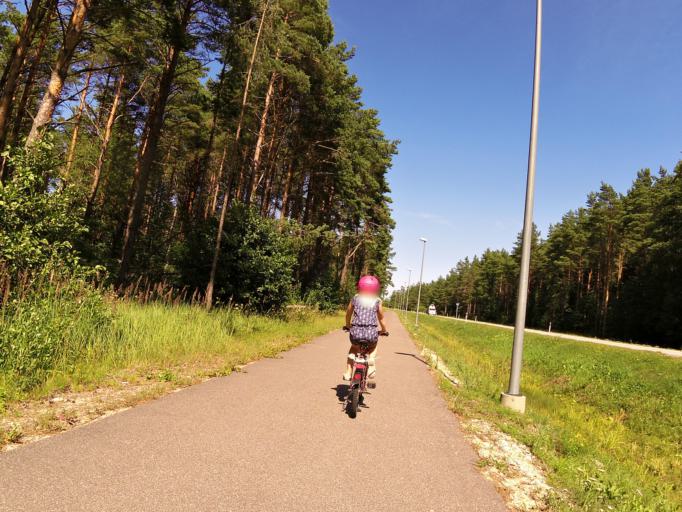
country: EE
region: Hiiumaa
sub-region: Kaerdla linn
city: Kardla
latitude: 58.9785
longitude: 22.5051
